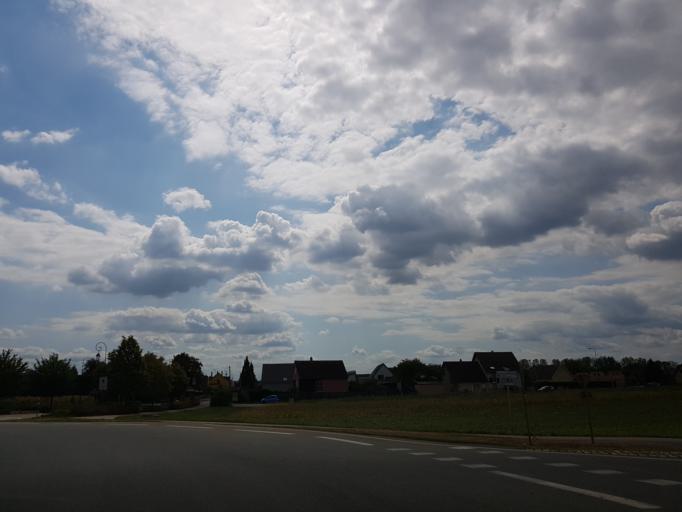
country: FR
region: Alsace
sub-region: Departement du Haut-Rhin
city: Sausheim
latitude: 47.7961
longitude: 7.3723
